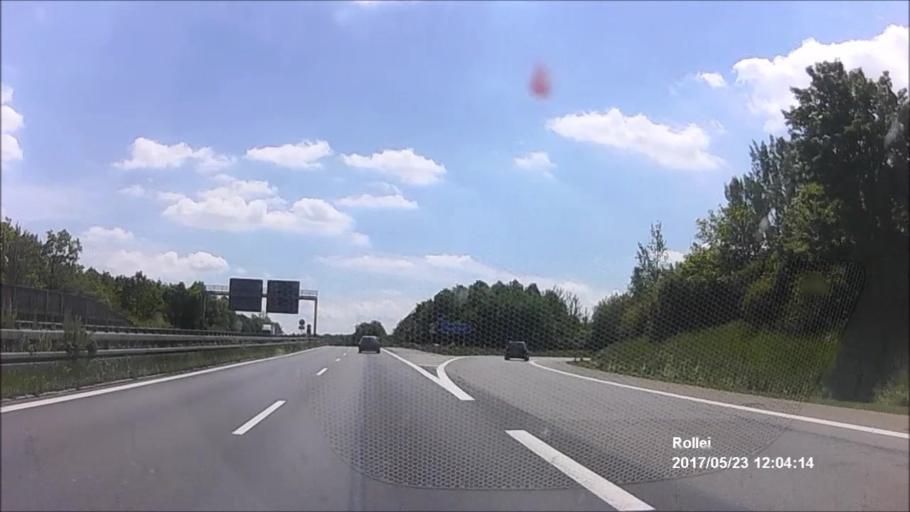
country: DE
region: Bavaria
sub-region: Upper Palatinate
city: Pentling
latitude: 48.9794
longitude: 12.0633
